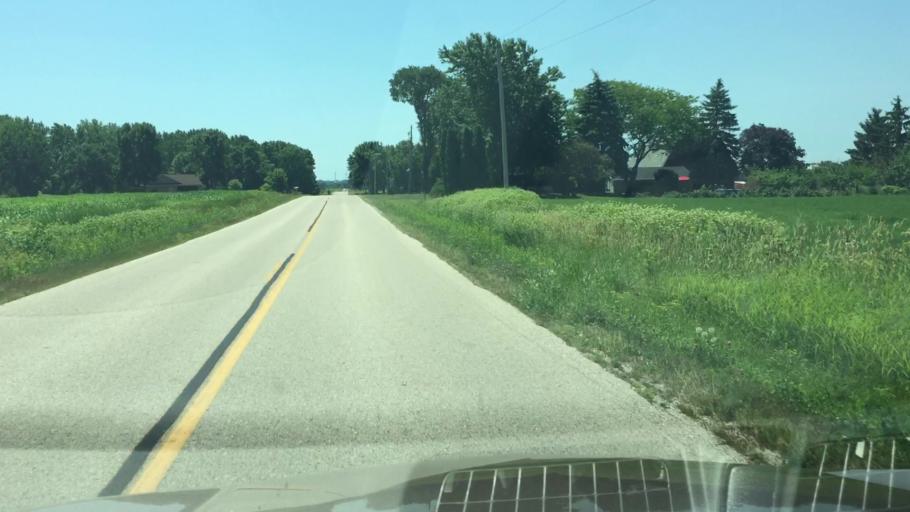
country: US
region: Wisconsin
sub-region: Fond du Lac County
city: Saint Peter
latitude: 43.9643
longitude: -88.3116
